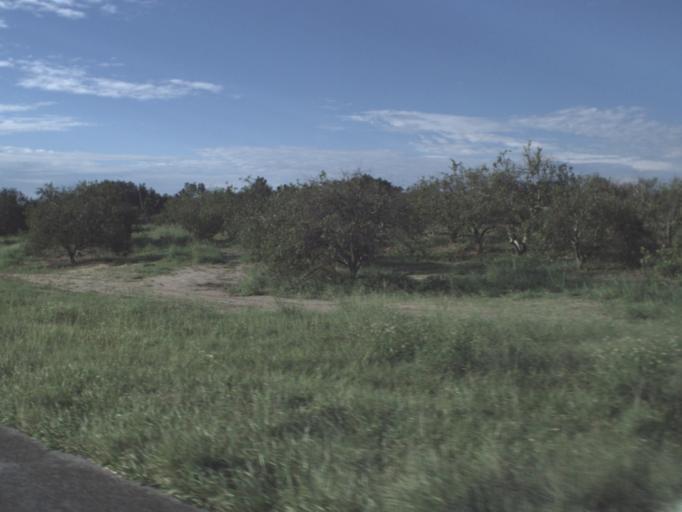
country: US
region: Florida
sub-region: Highlands County
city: Lake Placid
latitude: 27.2565
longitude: -81.3425
